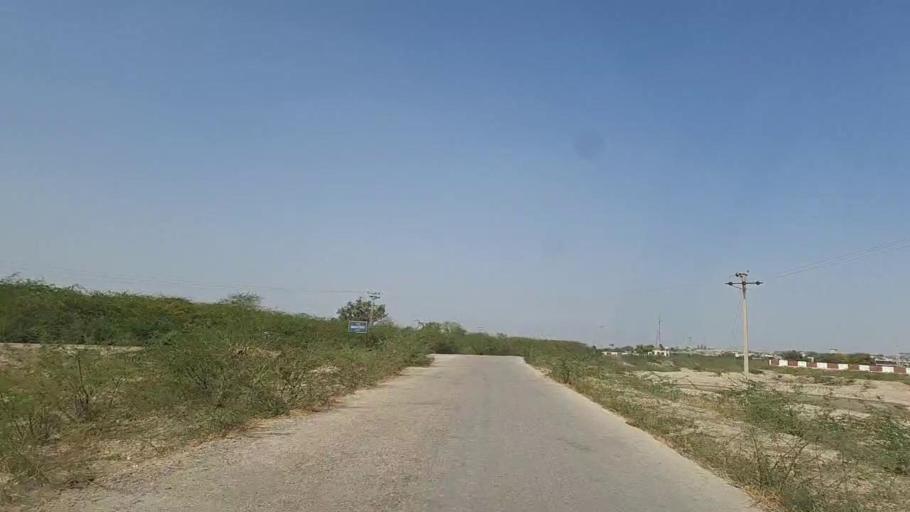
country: PK
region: Sindh
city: Naukot
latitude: 24.6501
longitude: 69.2879
